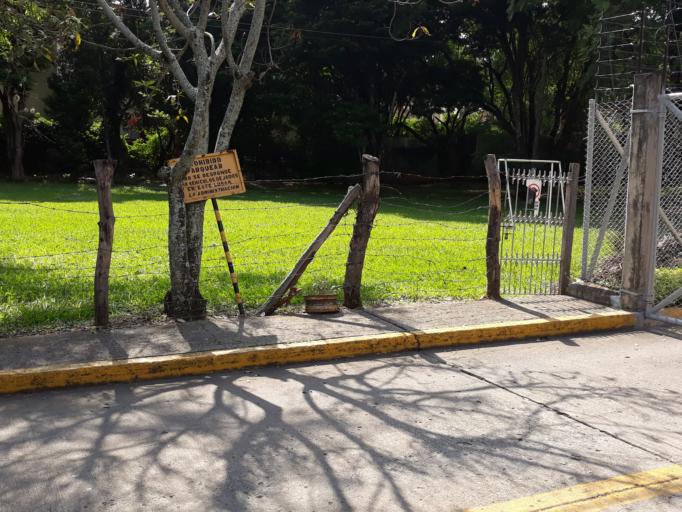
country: CO
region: Valle del Cauca
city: Cali
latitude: 3.3992
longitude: -76.5529
